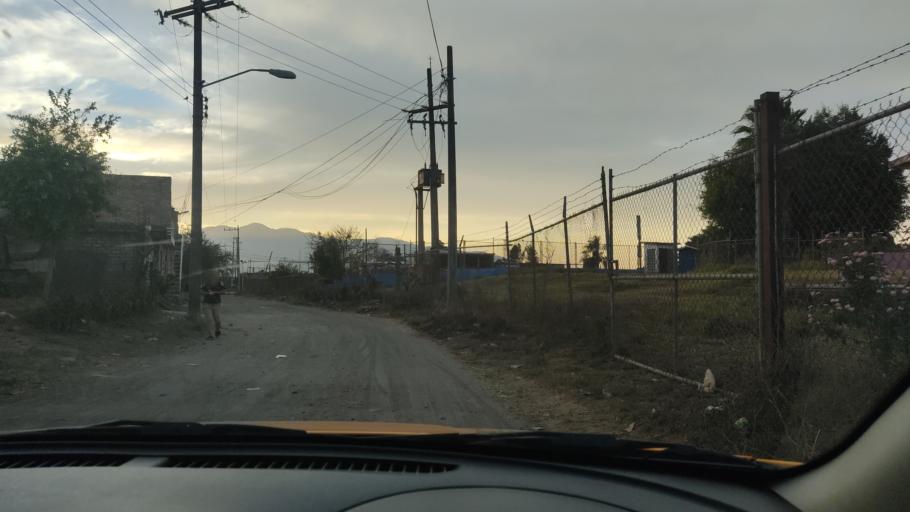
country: MX
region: Nayarit
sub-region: Tepic
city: La Corregidora
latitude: 21.4617
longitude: -104.8279
